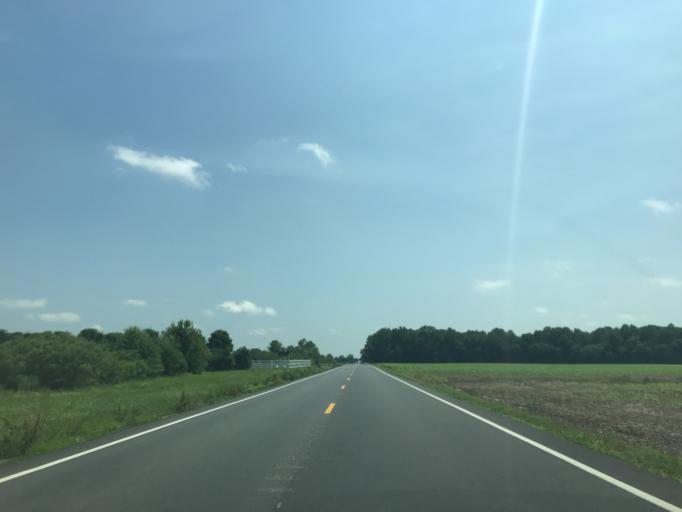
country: US
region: Maryland
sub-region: Dorchester County
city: Hurlock
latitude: 38.6074
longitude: -75.7795
